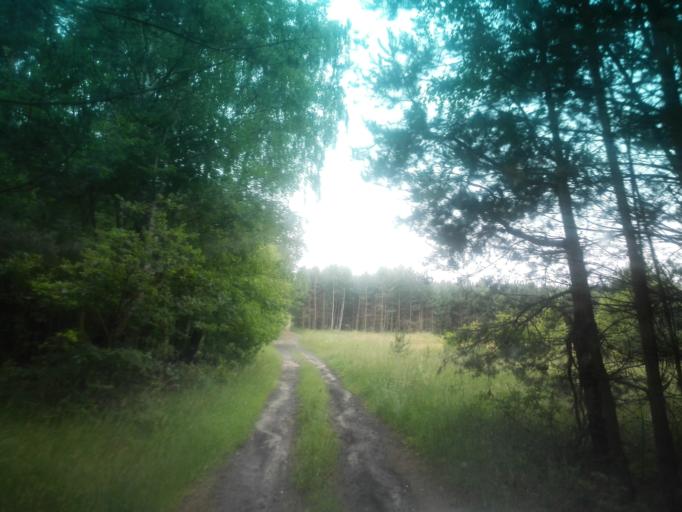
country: PL
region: Silesian Voivodeship
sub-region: Powiat czestochowski
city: Olsztyn
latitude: 50.7902
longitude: 19.2579
